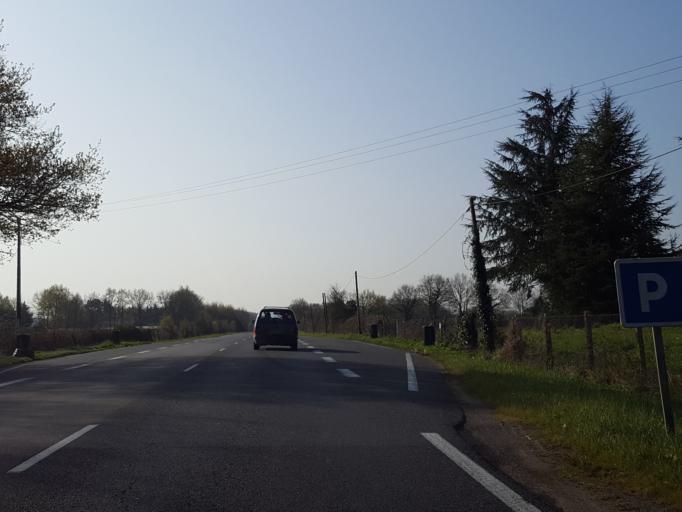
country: FR
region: Pays de la Loire
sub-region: Departement de la Loire-Atlantique
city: Geneston
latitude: 47.0822
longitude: -1.5256
